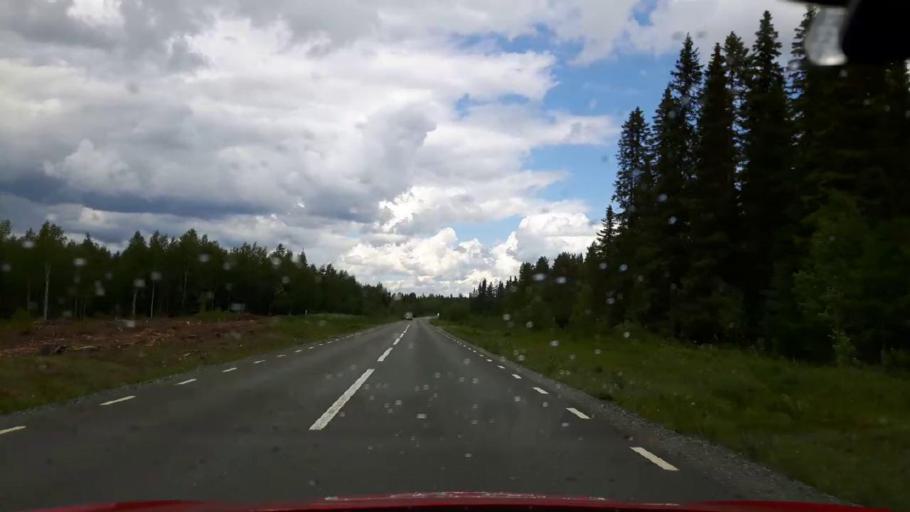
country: SE
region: Jaemtland
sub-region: Krokoms Kommun
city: Krokom
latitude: 63.5840
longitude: 14.2931
